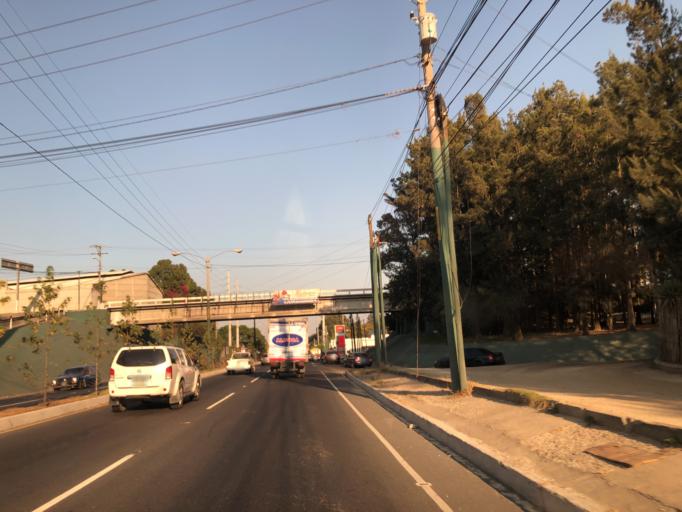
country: GT
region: Guatemala
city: Mixco
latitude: 14.6277
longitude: -90.6024
